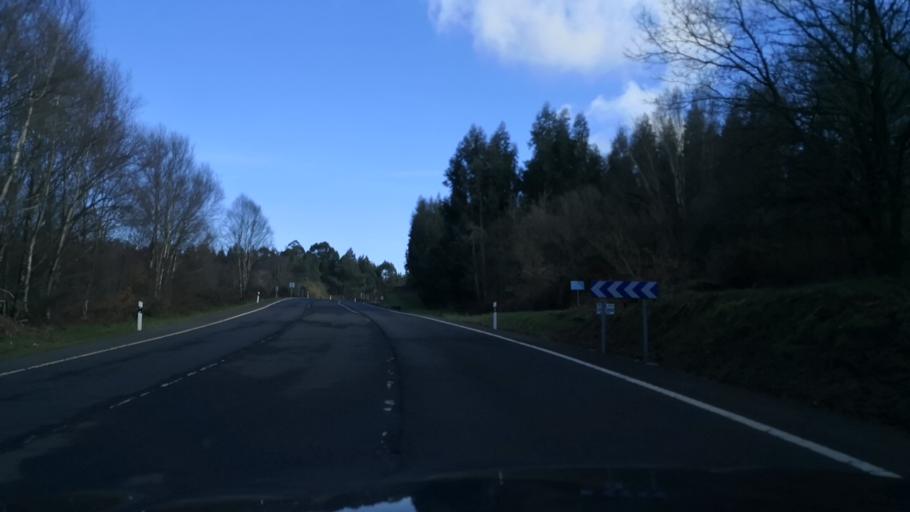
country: ES
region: Galicia
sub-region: Provincia da Coruna
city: Ribeira
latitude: 42.7109
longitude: -8.3570
